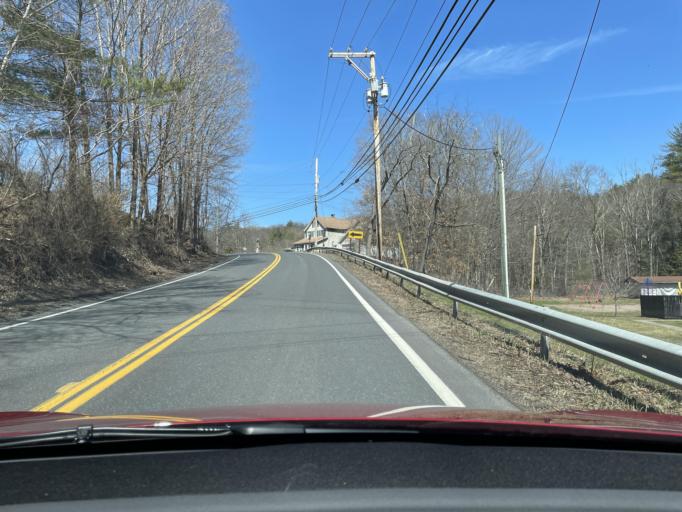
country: US
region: New York
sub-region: Ulster County
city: Lake Katrine
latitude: 41.9863
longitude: -74.0340
